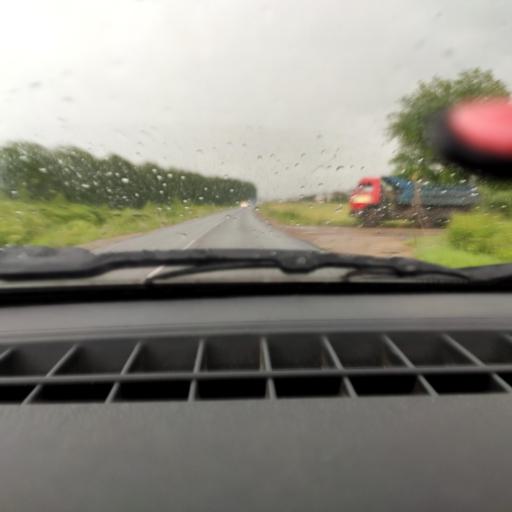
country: RU
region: Bashkortostan
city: Kabakovo
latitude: 54.6010
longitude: 56.2030
